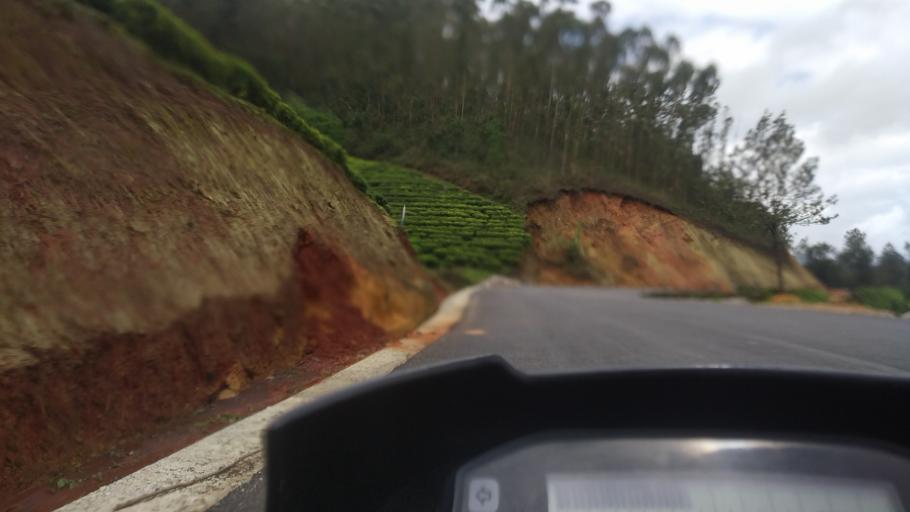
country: IN
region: Kerala
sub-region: Idukki
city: Munnar
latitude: 10.0760
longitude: 77.0887
